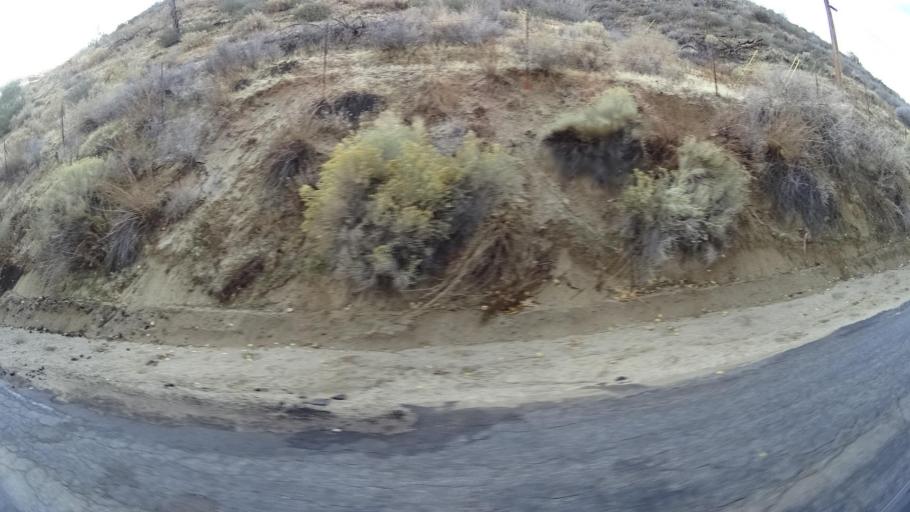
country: US
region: California
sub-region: Kern County
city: Tehachapi
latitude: 35.0877
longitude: -118.3164
